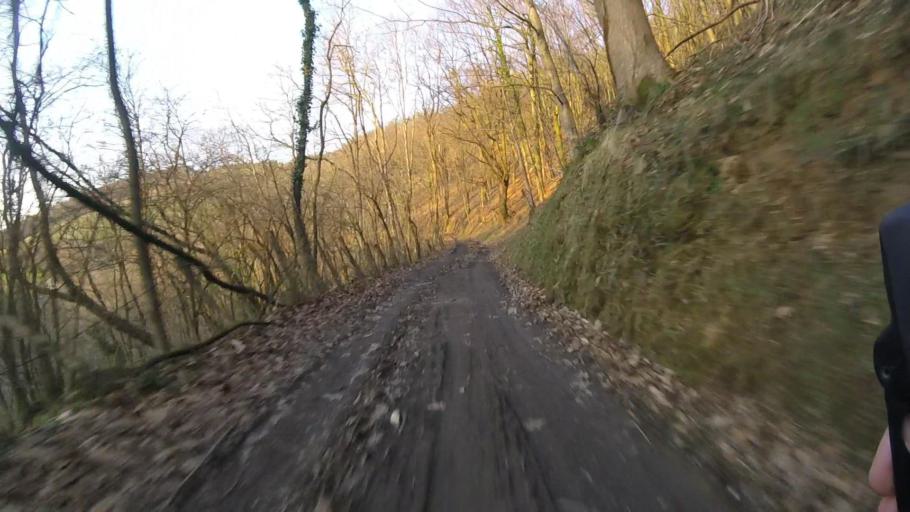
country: ES
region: Basque Country
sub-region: Provincia de Guipuzcoa
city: Errenteria
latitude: 43.2695
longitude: -1.8555
